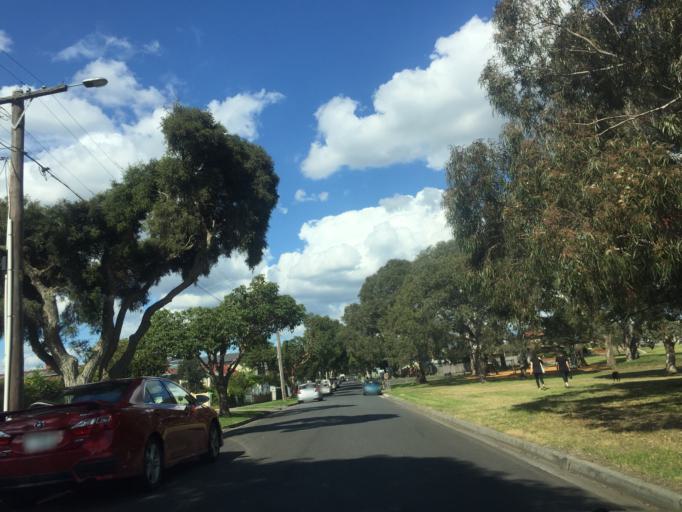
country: AU
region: Victoria
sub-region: Darebin
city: Kingsbury
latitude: -37.7166
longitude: 145.0296
